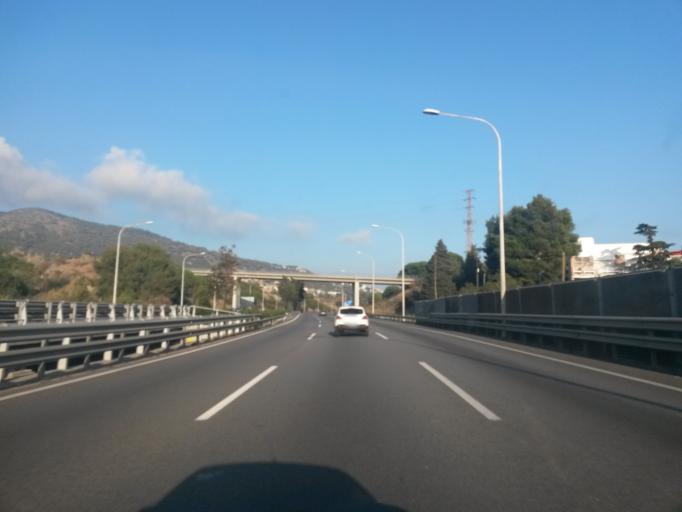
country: ES
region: Catalonia
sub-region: Provincia de Barcelona
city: El Masnou
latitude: 41.4885
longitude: 2.3226
